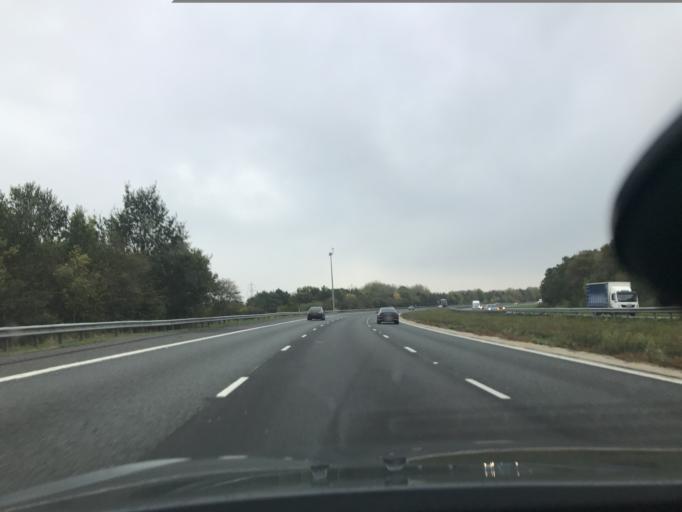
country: GB
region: England
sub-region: Oxfordshire
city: Wheatley
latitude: 51.7929
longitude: -1.0856
